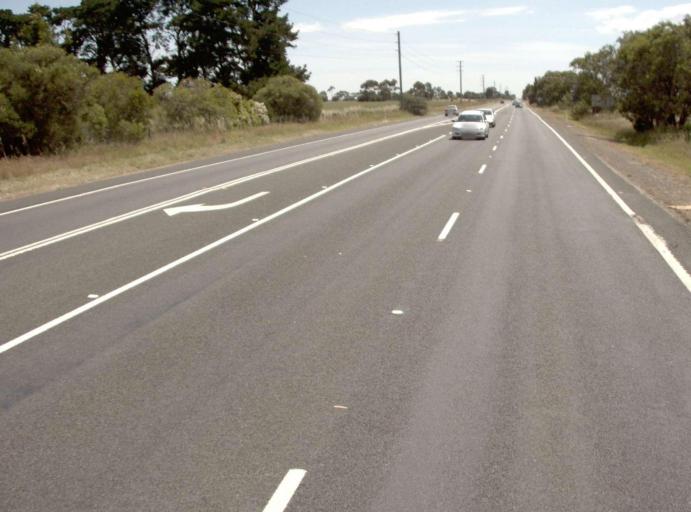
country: AU
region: Victoria
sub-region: Wellington
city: Sale
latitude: -38.1040
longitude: 146.9250
